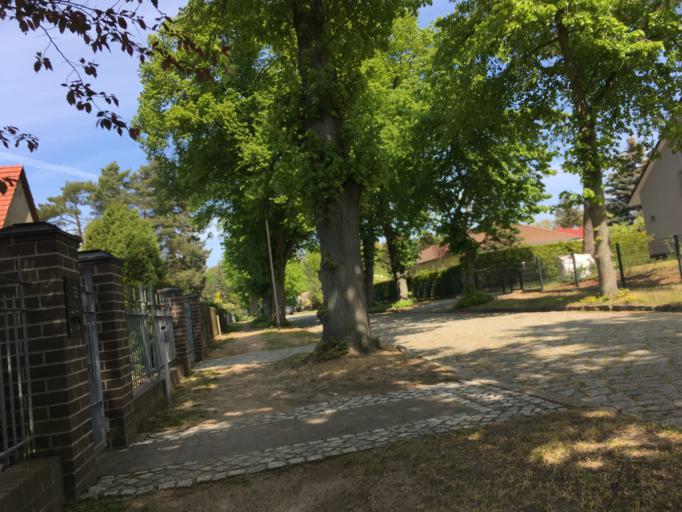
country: DE
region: Berlin
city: Blankenfelde
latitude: 52.6518
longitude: 13.3863
